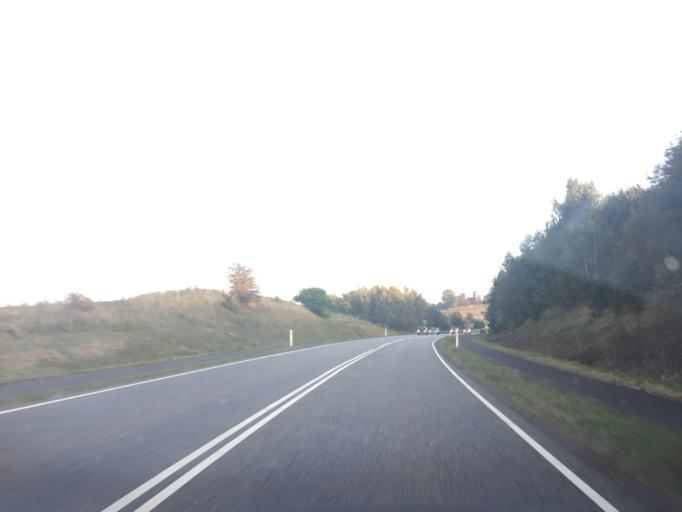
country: DK
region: Zealand
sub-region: Lejre Kommune
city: Kirke Hvalso
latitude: 55.5831
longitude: 11.9090
